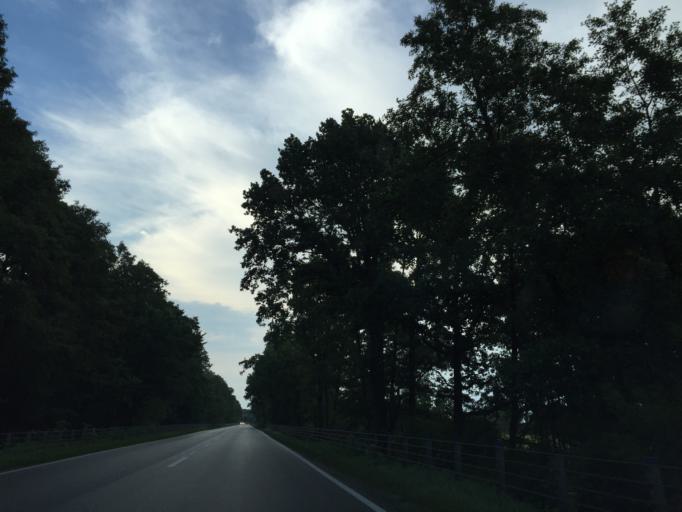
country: PL
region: Masovian Voivodeship
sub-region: Powiat ostrowski
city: Brok
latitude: 52.6821
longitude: 21.8513
